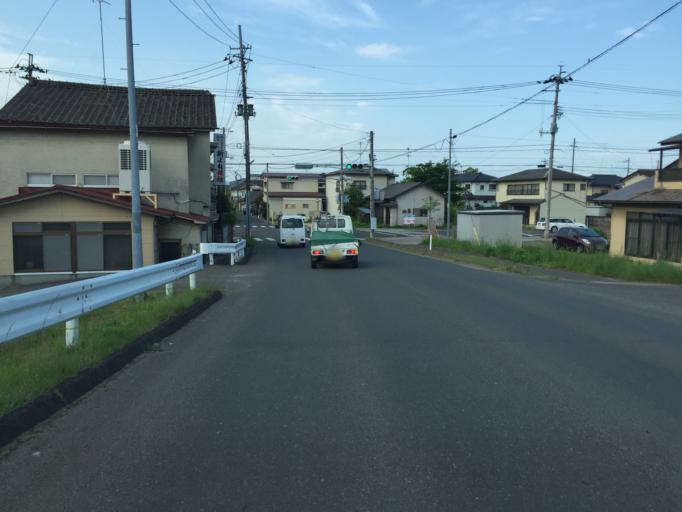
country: JP
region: Fukushima
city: Yanagawamachi-saiwaicho
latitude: 37.8560
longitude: 140.6048
